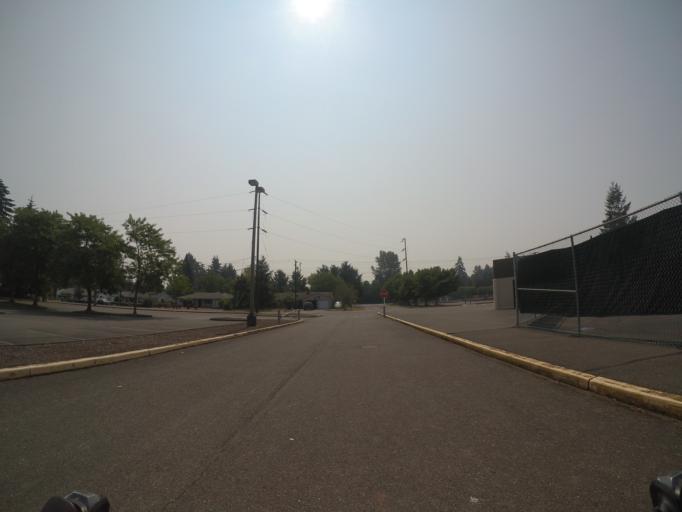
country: US
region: Washington
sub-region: Pierce County
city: Lakewood
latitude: 47.1572
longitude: -122.5160
